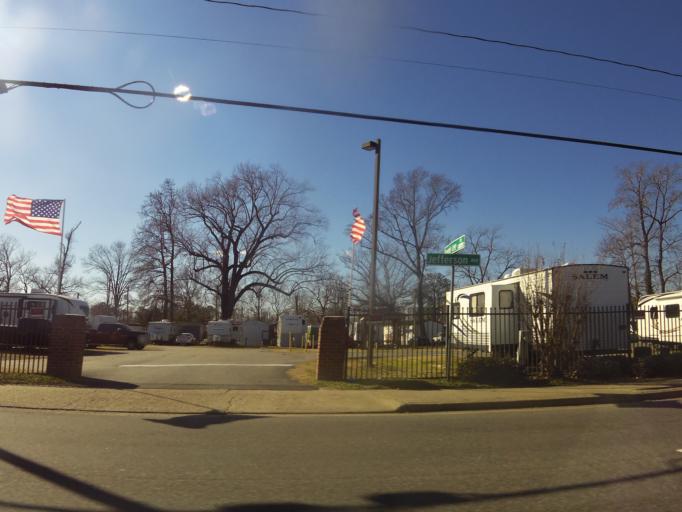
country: US
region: Virginia
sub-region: City of Newport News
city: Newport News
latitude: 37.0146
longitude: -76.4416
